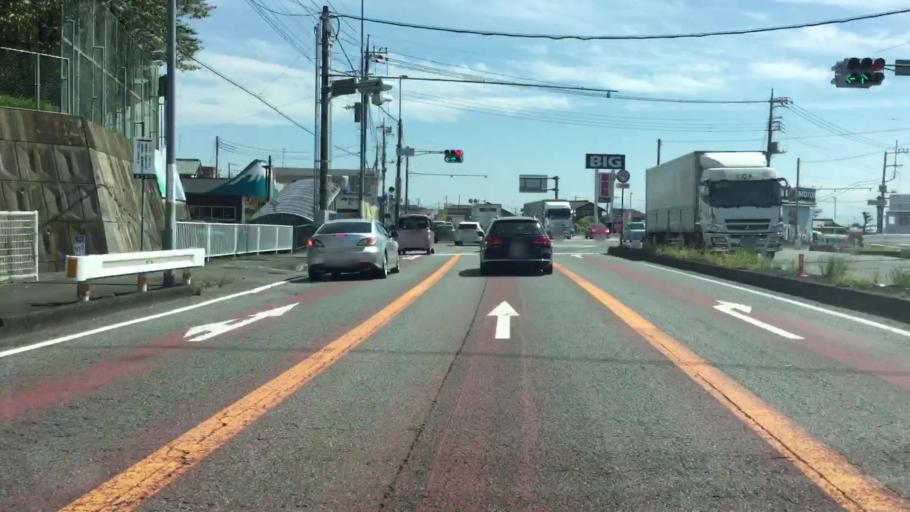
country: JP
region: Shizuoka
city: Fujinomiya
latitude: 35.2247
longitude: 138.6276
